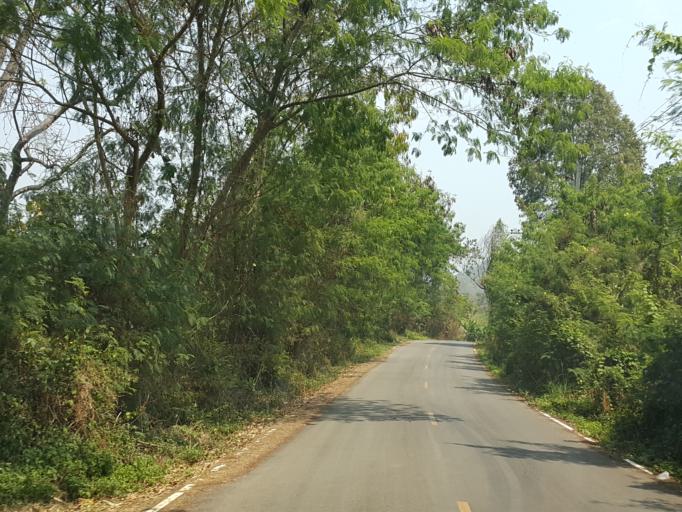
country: TH
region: Lampang
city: Mueang Pan
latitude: 18.8200
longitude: 99.4479
